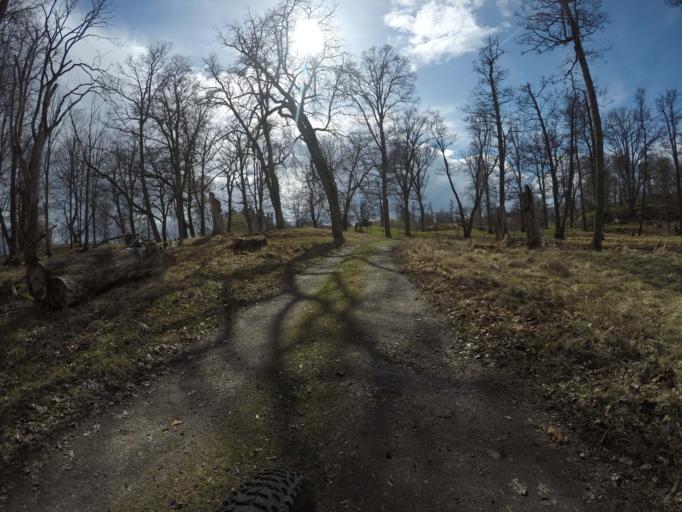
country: SE
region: Vaestmanland
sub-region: Kungsors Kommun
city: Kungsoer
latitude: 59.2723
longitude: 16.1296
